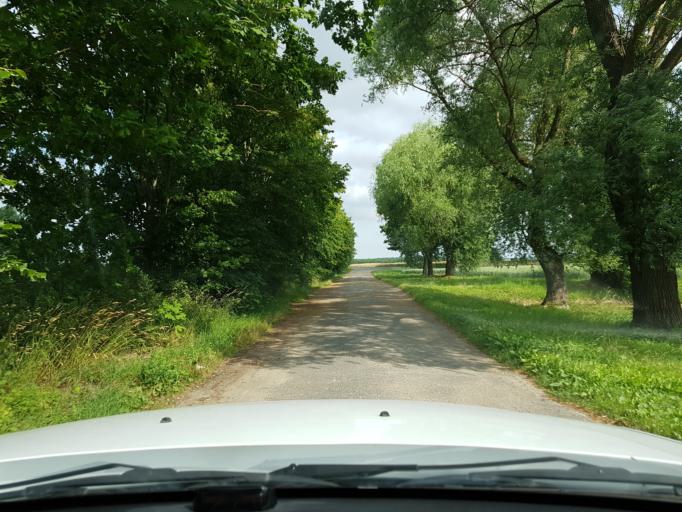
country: PL
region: West Pomeranian Voivodeship
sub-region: Powiat gryfinski
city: Banie
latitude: 53.1282
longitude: 14.5975
